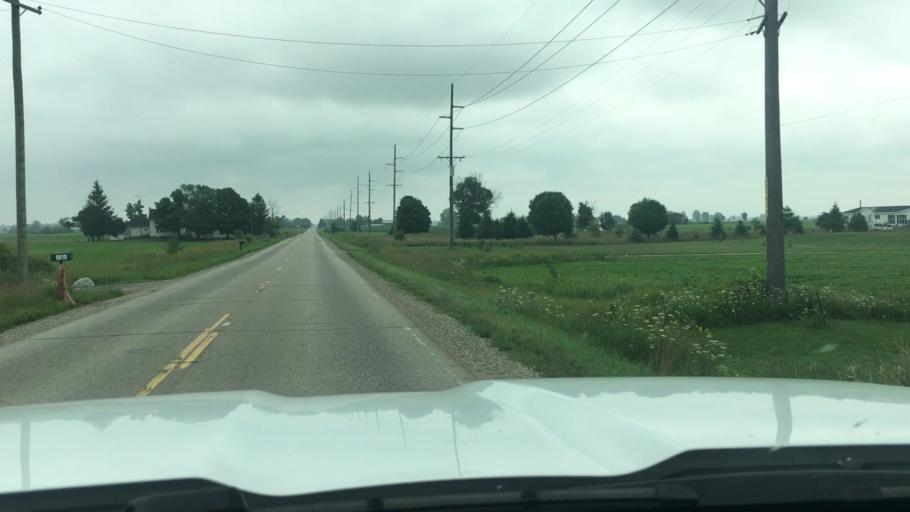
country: US
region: Michigan
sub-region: Sanilac County
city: Brown City
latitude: 43.2560
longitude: -83.0151
